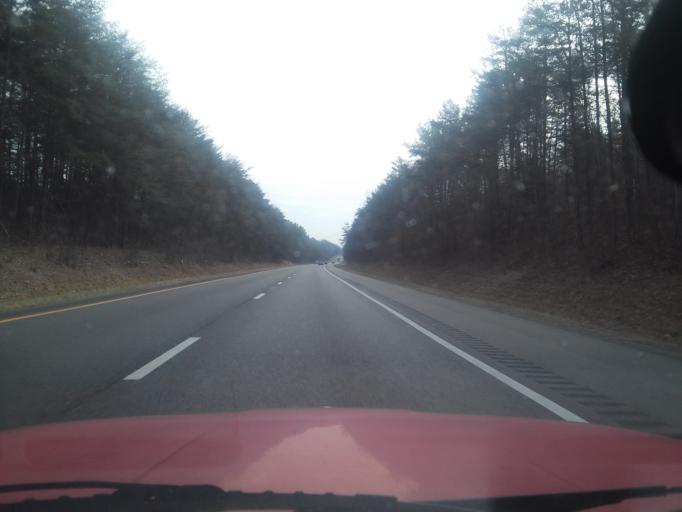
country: US
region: Virginia
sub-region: Goochland County
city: Goochland
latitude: 37.7905
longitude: -77.9001
